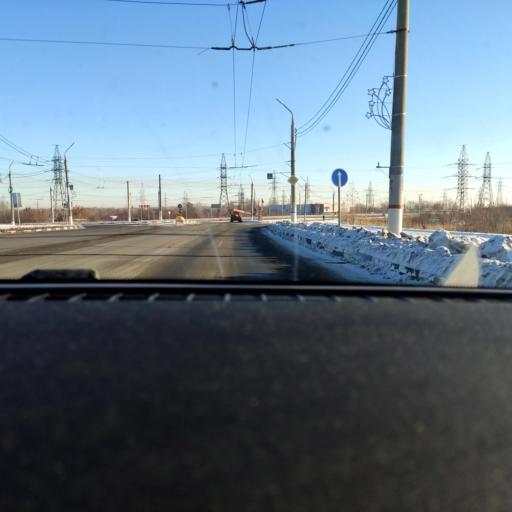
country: RU
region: Samara
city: Novokuybyshevsk
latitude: 53.0870
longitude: 49.9958
